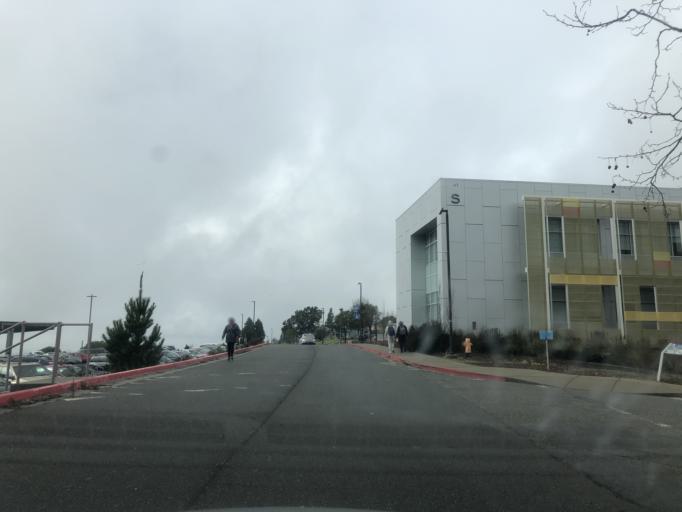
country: US
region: California
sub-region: Contra Costa County
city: Moraga
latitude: 37.7875
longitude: -122.1657
